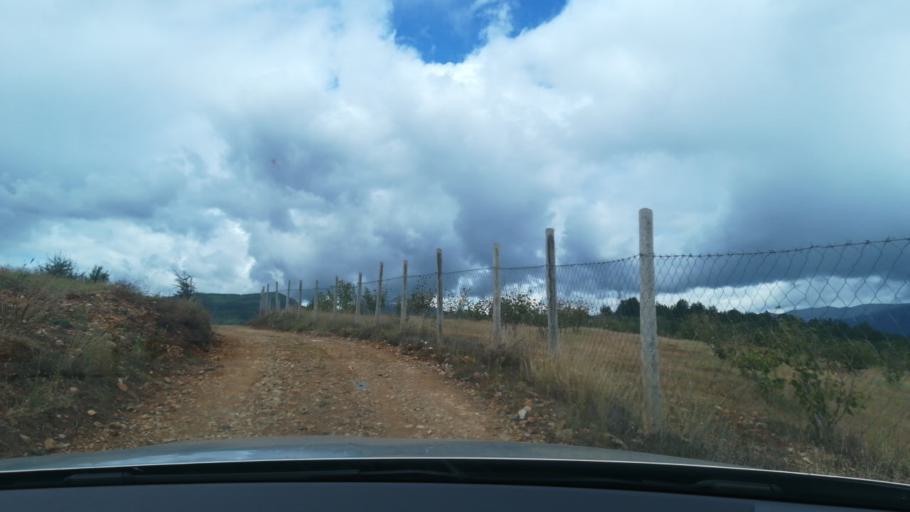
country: MK
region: Makedonska Kamenica
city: Makedonska Kamenica
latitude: 42.0073
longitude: 22.6037
